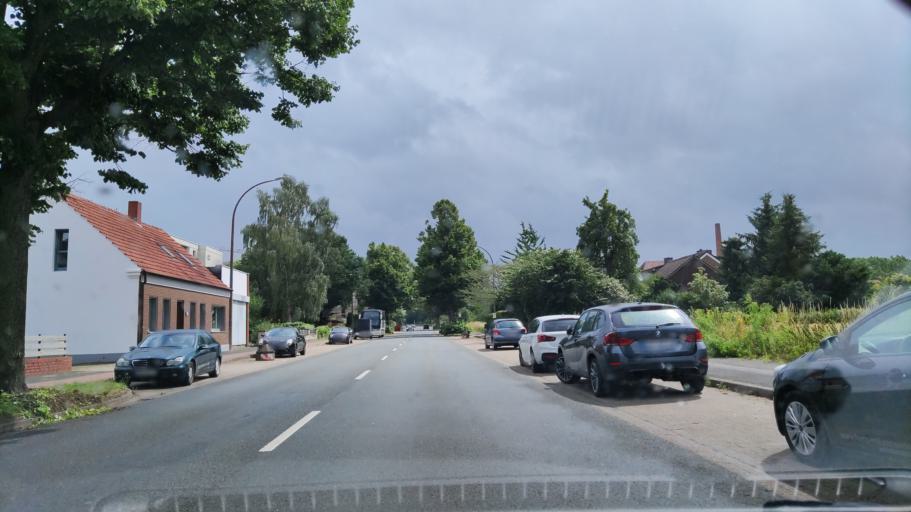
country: DE
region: North Rhine-Westphalia
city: Ahlen
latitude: 51.7556
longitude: 7.8798
